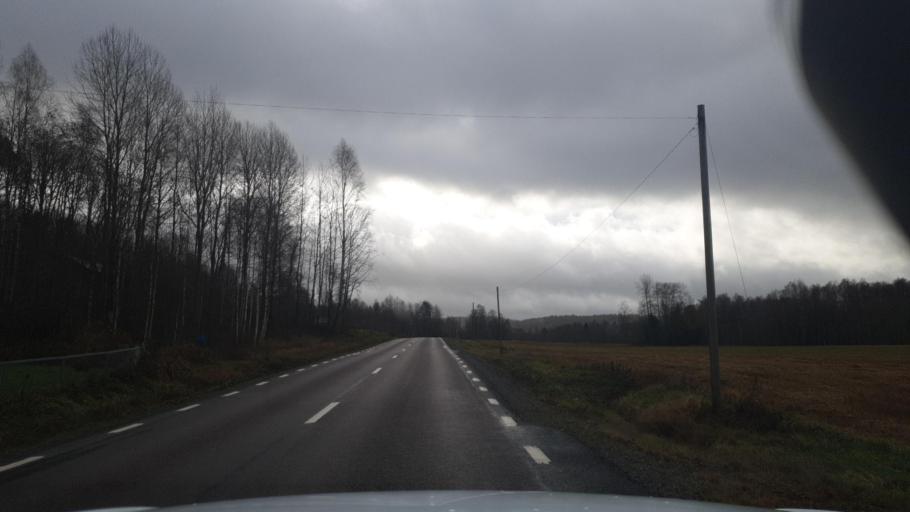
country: SE
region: Vaermland
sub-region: Arjangs Kommun
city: Arjaeng
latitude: 59.6080
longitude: 12.1513
